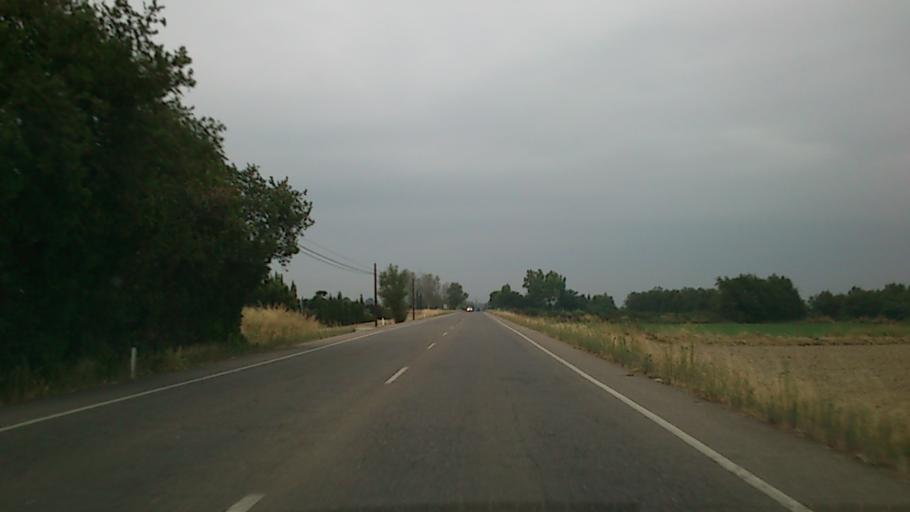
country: ES
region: Aragon
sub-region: Provincia de Zaragoza
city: Villanueva de Gallego
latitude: 41.7490
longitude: -0.8021
